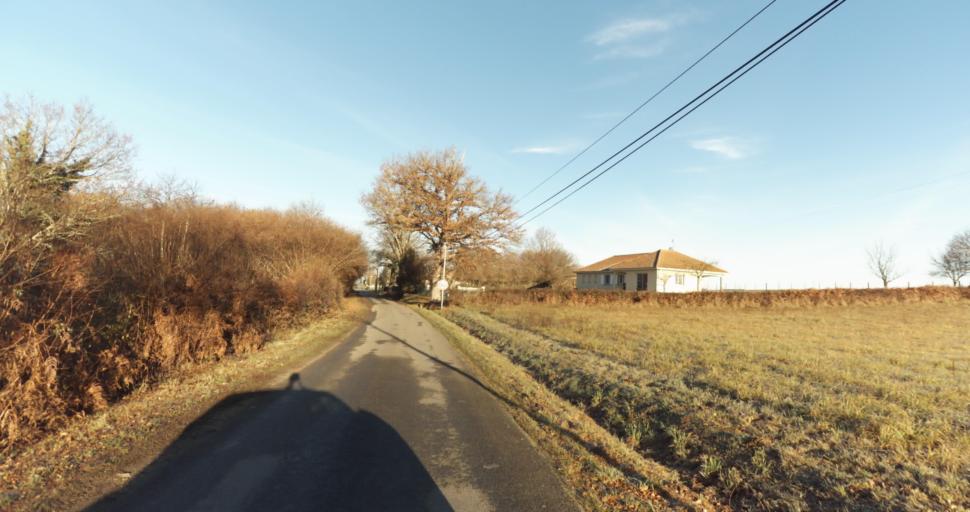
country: FR
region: Limousin
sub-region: Departement de la Haute-Vienne
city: Aixe-sur-Vienne
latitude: 45.8183
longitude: 1.1414
